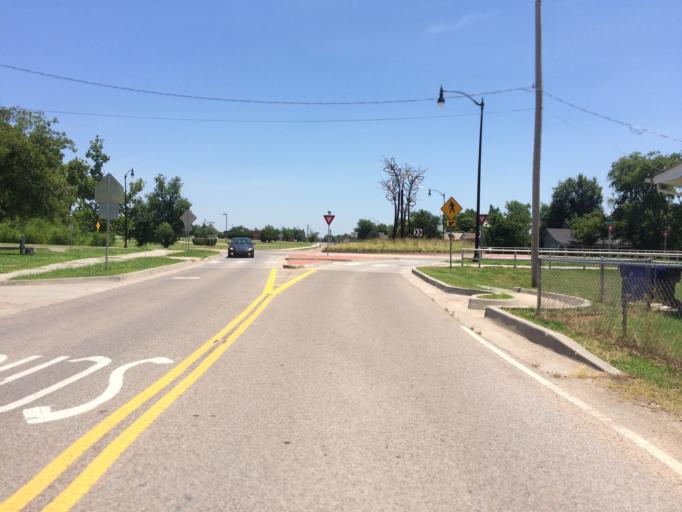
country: US
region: Oklahoma
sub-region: Cleveland County
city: Norman
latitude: 35.2257
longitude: -97.4332
